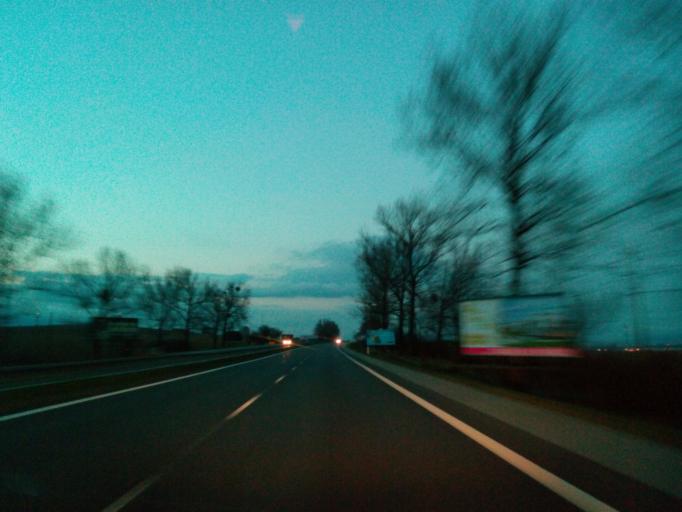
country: SK
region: Kosicky
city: Kosice
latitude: 48.6683
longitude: 21.2100
